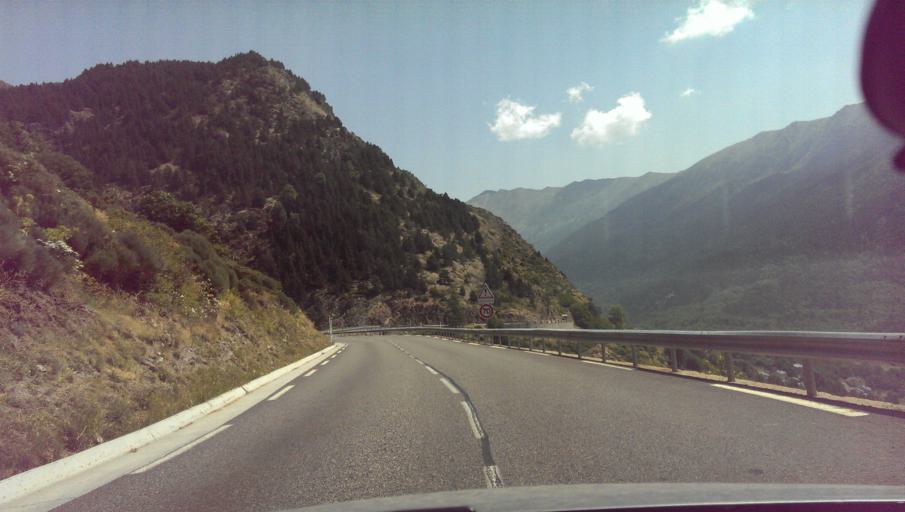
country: AD
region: Encamp
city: Pas de la Casa
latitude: 42.5513
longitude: 1.8305
